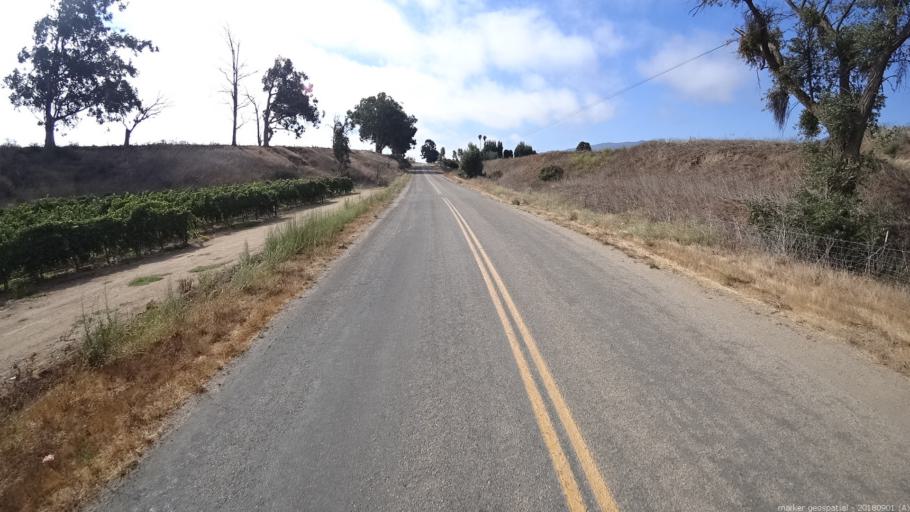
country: US
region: California
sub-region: Monterey County
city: Soledad
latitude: 36.3745
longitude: -121.3375
